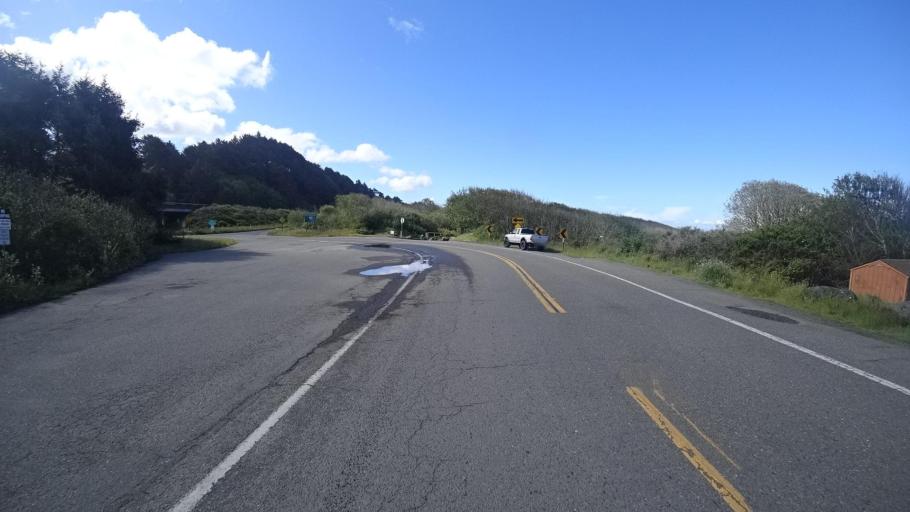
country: US
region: California
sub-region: Humboldt County
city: McKinleyville
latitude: 40.9947
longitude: -124.1141
